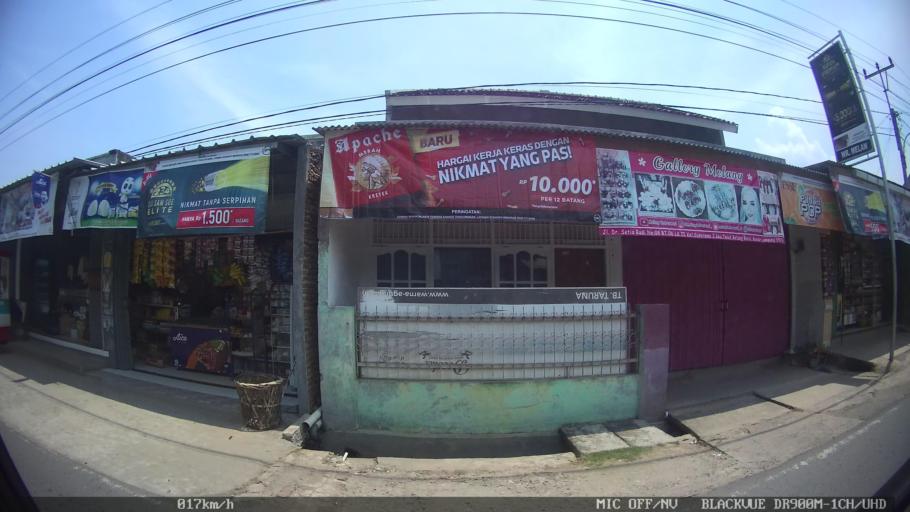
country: ID
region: Lampung
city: Bandarlampung
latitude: -5.4406
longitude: 105.2412
